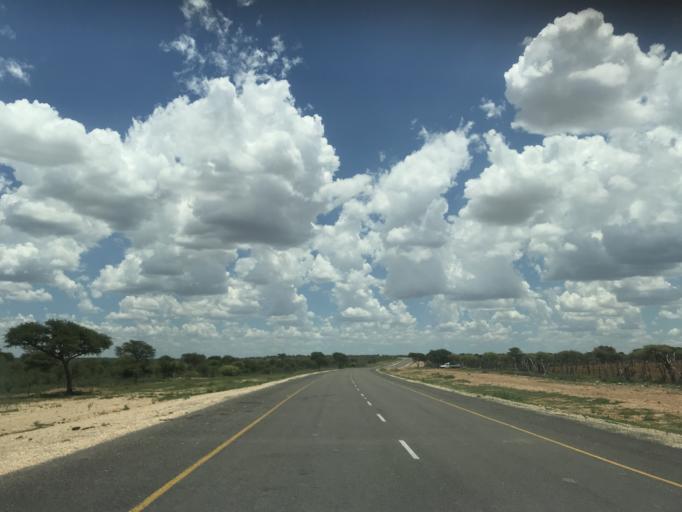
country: BW
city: Mabuli
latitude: -25.7962
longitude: 24.8838
